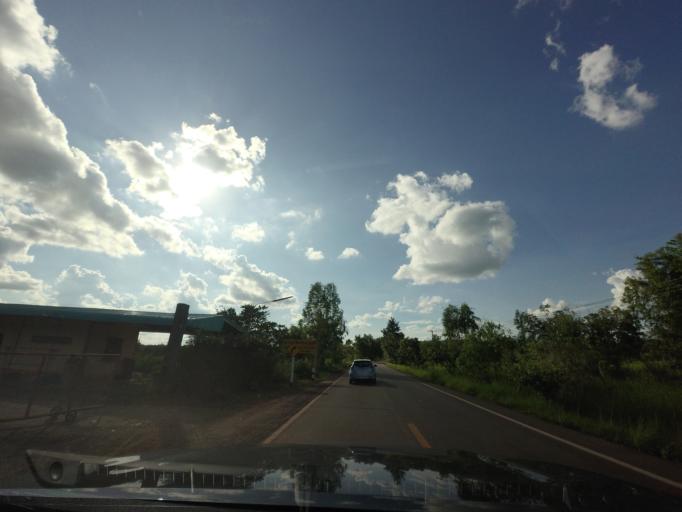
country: TH
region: Changwat Udon Thani
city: Ban Dung
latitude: 17.7436
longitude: 103.3075
